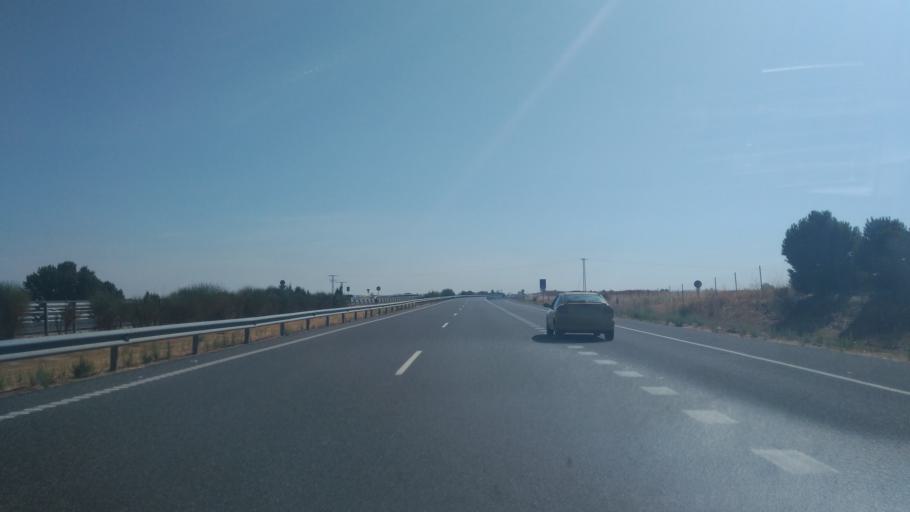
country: ES
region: Castille and Leon
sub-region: Provincia de Salamanca
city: Santa Marta de Tormes
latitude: 40.9445
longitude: -5.6071
